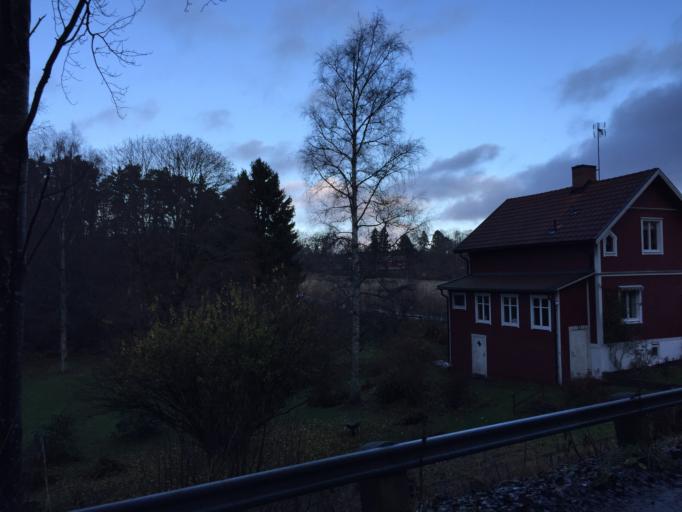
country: SE
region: Stockholm
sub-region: Salems Kommun
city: Ronninge
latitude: 59.1960
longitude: 17.7259
